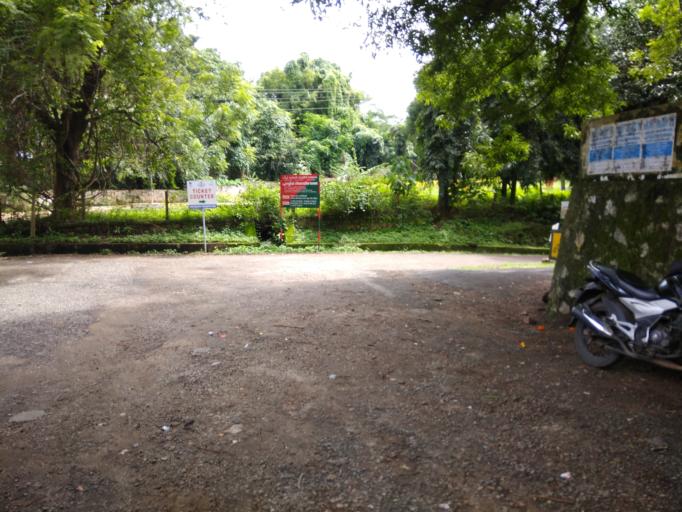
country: IN
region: Kerala
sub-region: Thrissur District
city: Trichur
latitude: 10.5286
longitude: 76.3678
